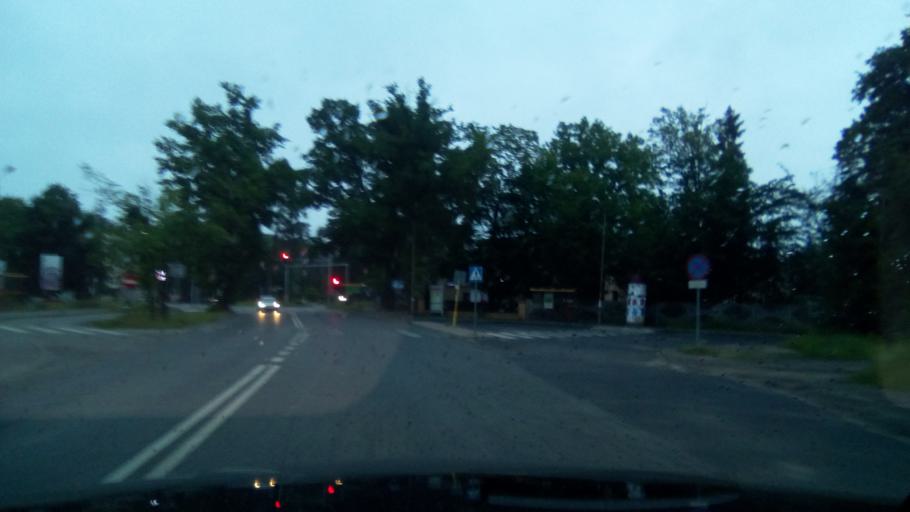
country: PL
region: Greater Poland Voivodeship
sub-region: Powiat poznanski
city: Kobylnica
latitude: 52.4453
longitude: 17.0764
